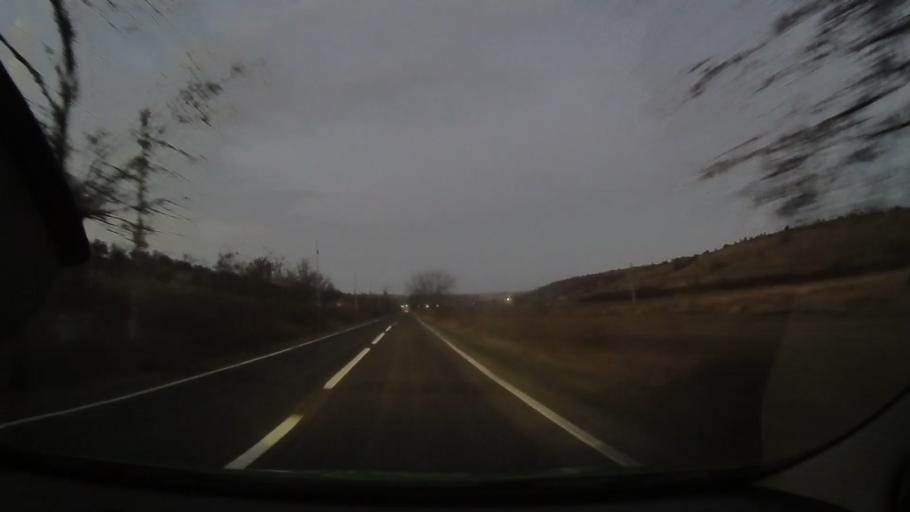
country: RO
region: Constanta
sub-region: Comuna Ion Corvin
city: Ion Corvin
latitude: 44.1032
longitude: 27.7992
